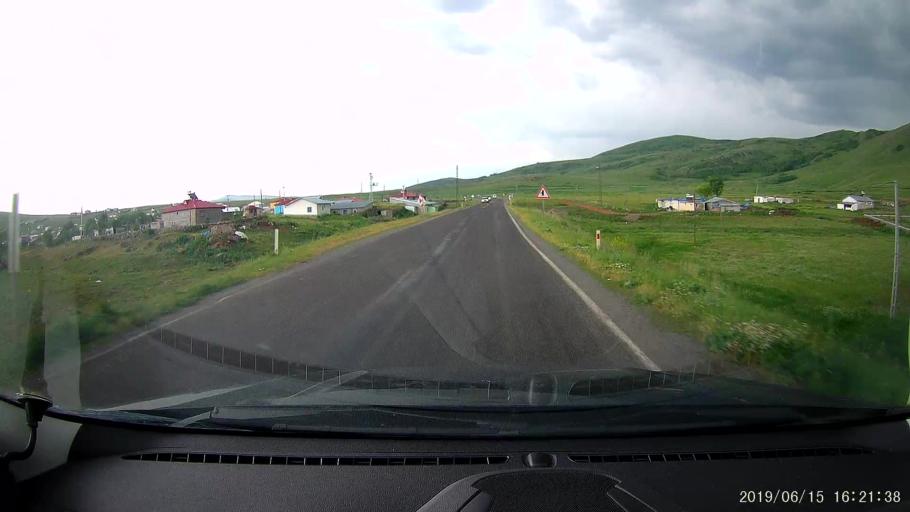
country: TR
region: Ardahan
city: Hanak
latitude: 41.1977
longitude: 42.8468
